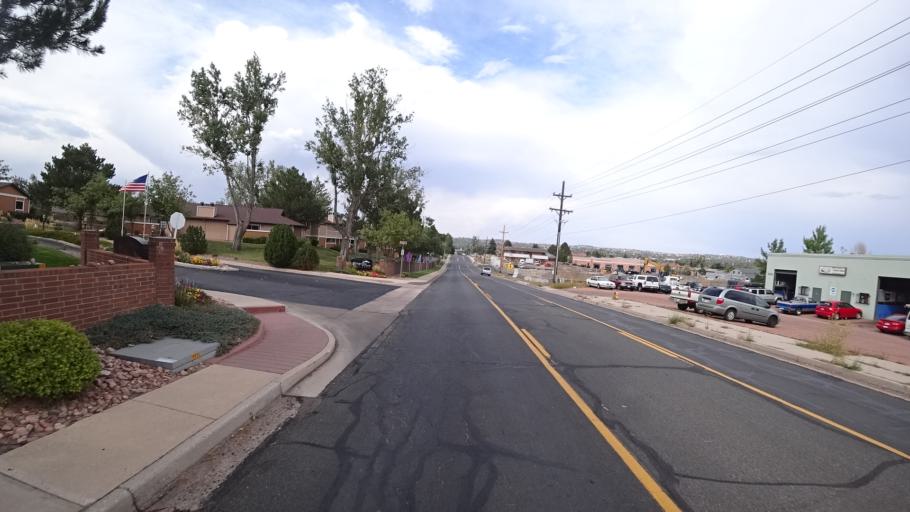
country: US
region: Colorado
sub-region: El Paso County
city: Cimarron Hills
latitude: 38.8809
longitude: -104.7610
